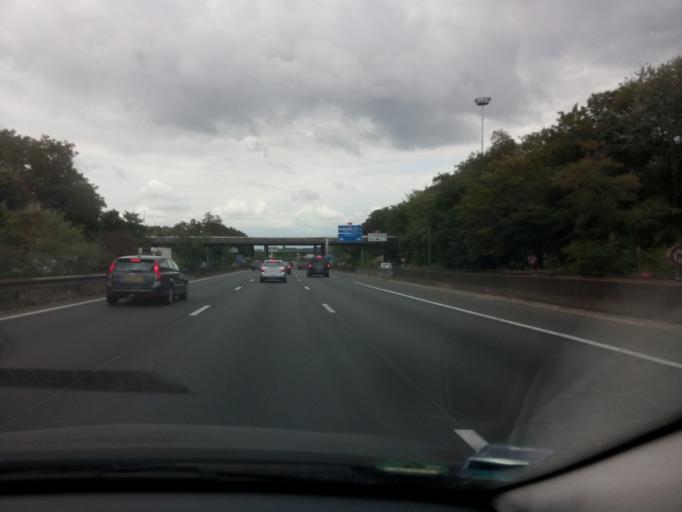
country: FR
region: Ile-de-France
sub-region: Departement de Seine-Saint-Denis
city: Le Blanc-Mesnil
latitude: 48.9491
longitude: 2.4753
